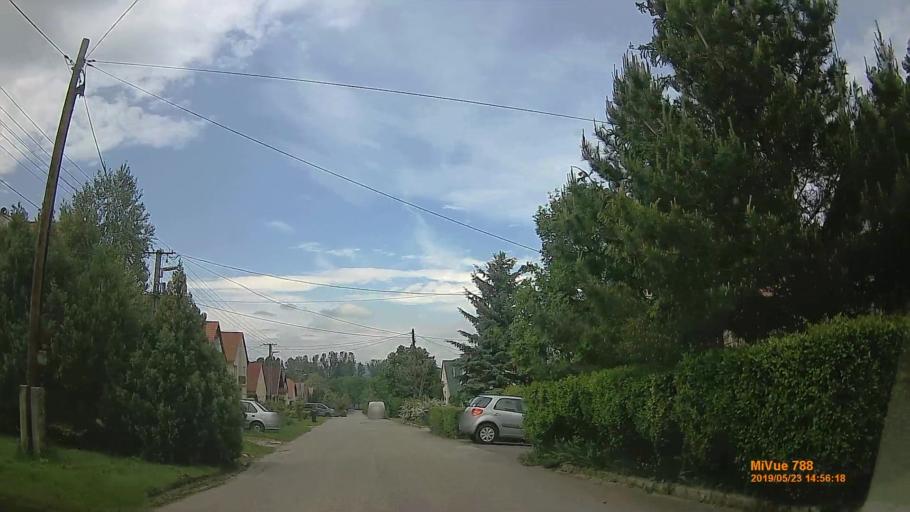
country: HU
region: Veszprem
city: Liter
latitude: 47.1233
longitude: 17.9568
